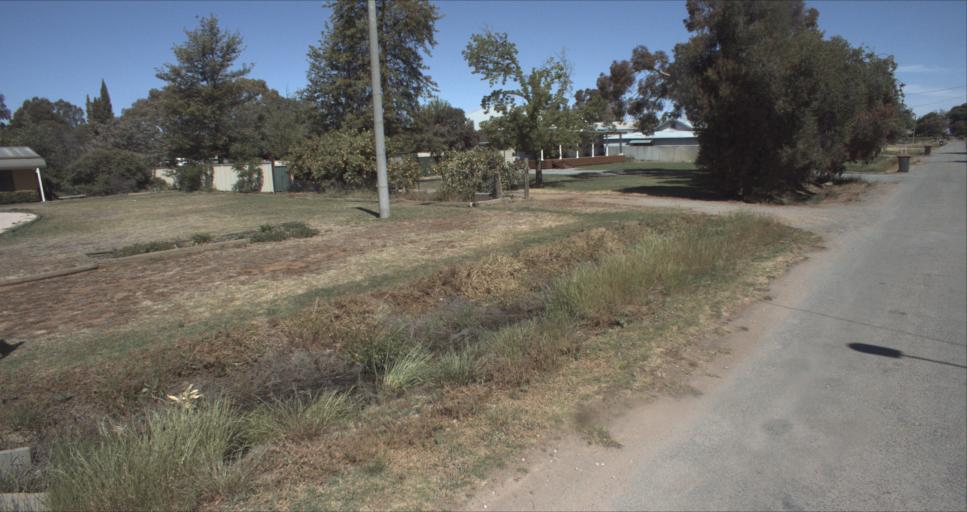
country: AU
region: New South Wales
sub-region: Leeton
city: Leeton
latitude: -34.5531
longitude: 146.3834
